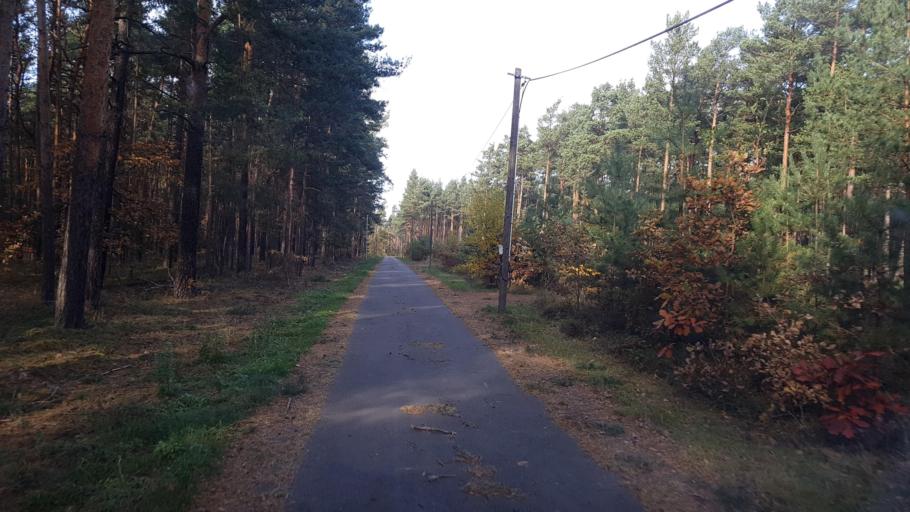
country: DE
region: Brandenburg
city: Tettau
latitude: 51.4244
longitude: 13.7616
